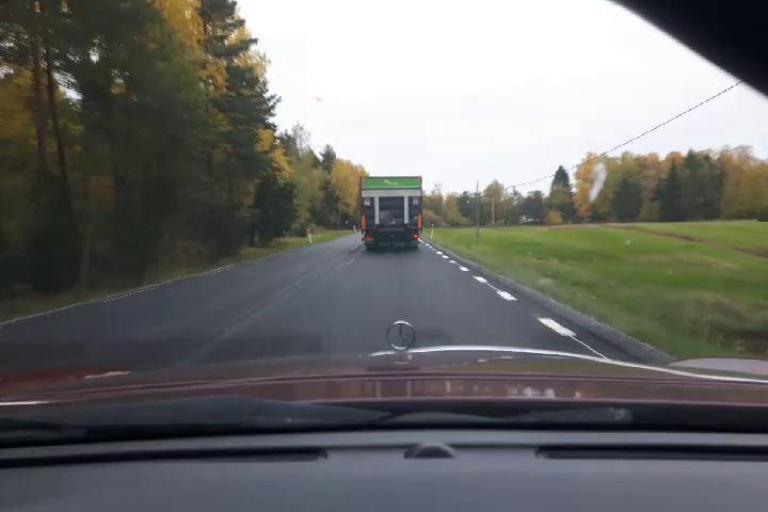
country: SE
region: Soedermanland
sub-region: Strangnas Kommun
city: Strangnas
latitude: 59.4279
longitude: 17.0257
